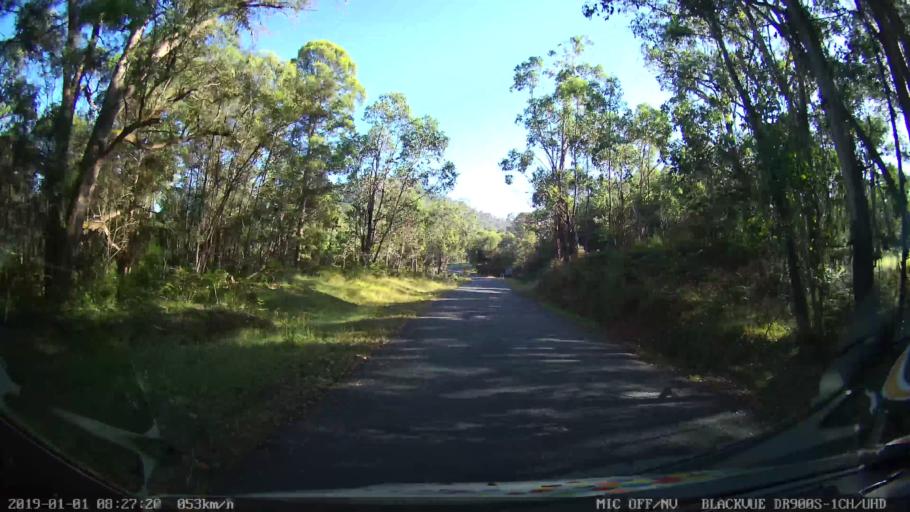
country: AU
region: New South Wales
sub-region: Snowy River
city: Jindabyne
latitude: -36.3823
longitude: 148.1835
